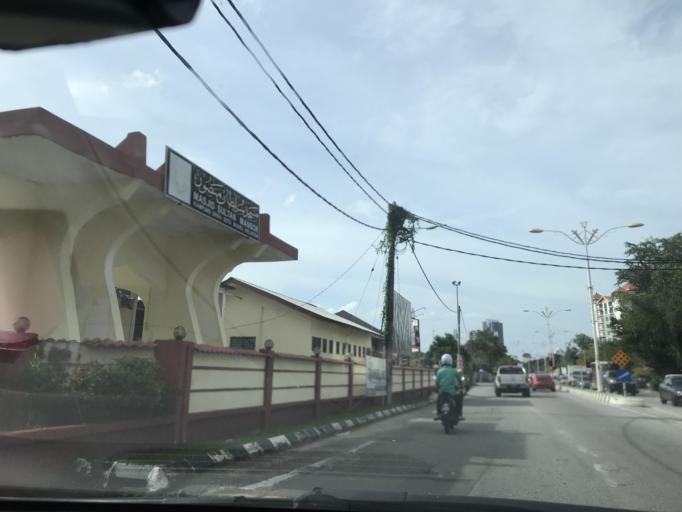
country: MY
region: Kelantan
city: Kota Bharu
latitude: 6.1086
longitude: 102.2368
